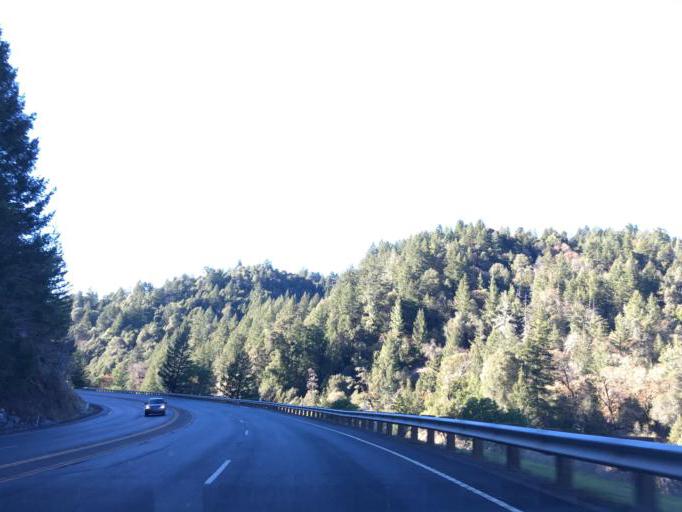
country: US
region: California
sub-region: Mendocino County
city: Laytonville
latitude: 39.8278
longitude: -123.5857
